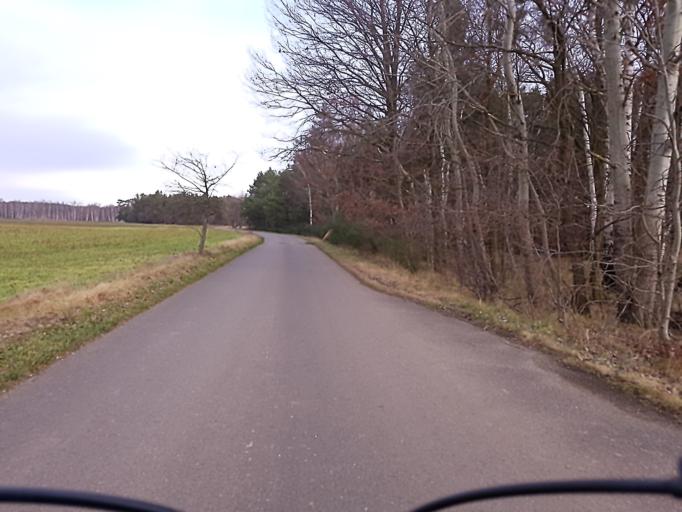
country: DE
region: Brandenburg
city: Schilda
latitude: 51.5723
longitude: 13.3936
